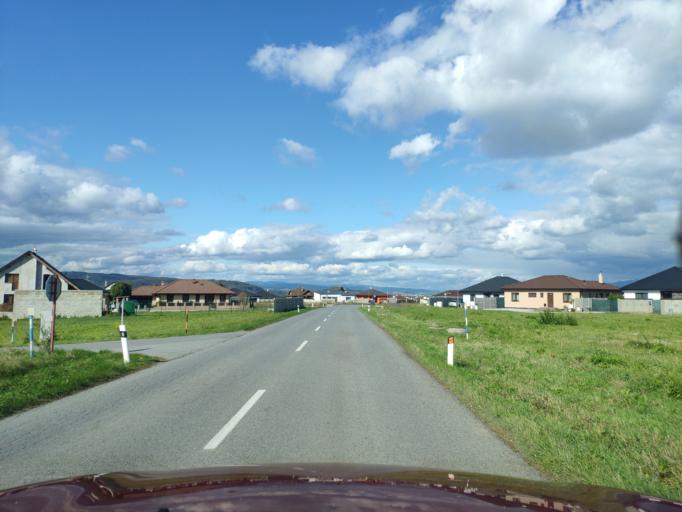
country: SK
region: Presovsky
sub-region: Okres Presov
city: Presov
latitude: 48.9618
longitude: 21.2865
